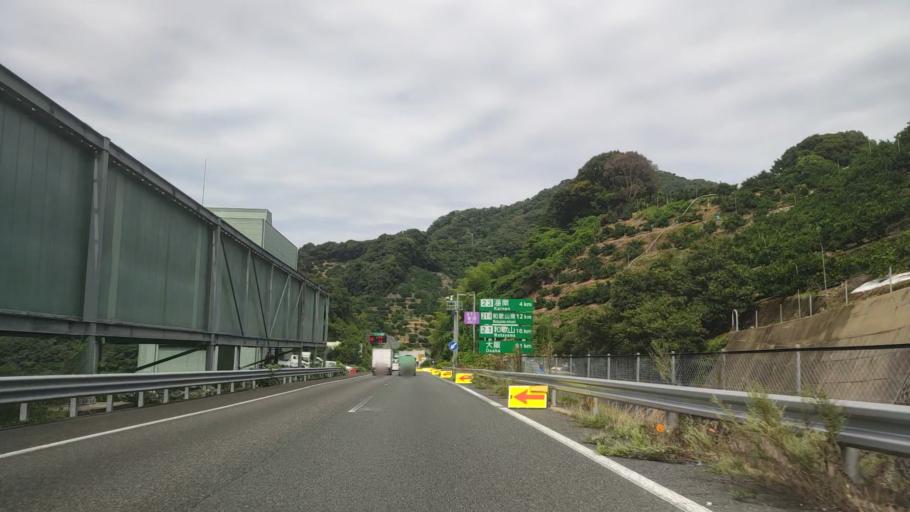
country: JP
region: Wakayama
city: Kainan
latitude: 34.1122
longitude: 135.2002
